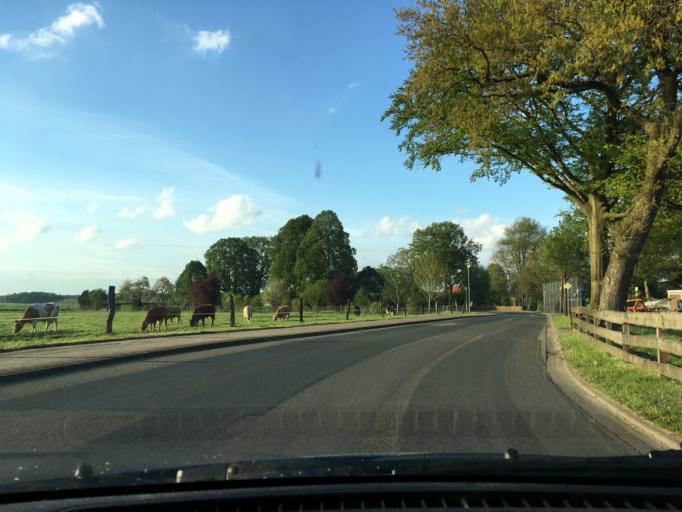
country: DE
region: Lower Saxony
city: Bergen
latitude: 52.8435
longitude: 9.9721
